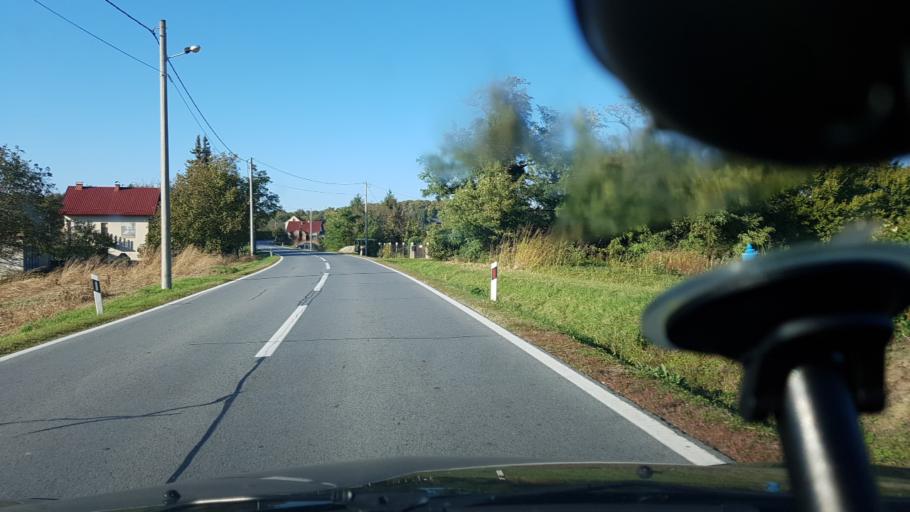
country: HR
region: Bjelovarsko-Bilogorska
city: Bjelovar
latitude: 45.9767
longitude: 16.8955
